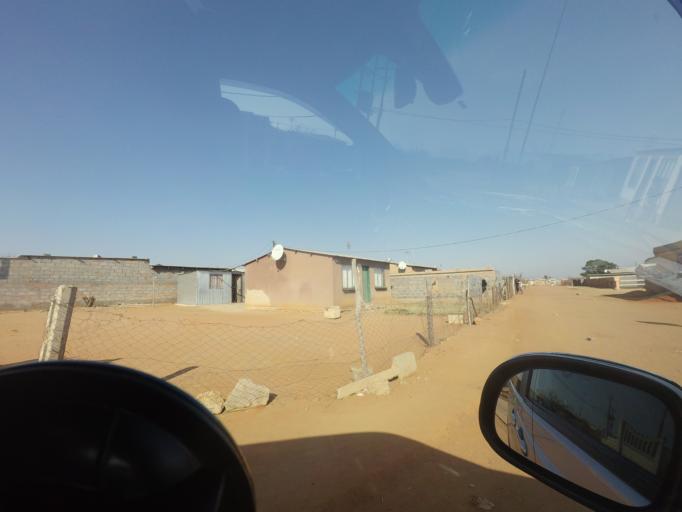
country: ZA
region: Gauteng
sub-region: Sedibeng District Municipality
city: Heidelberg
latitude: -26.5368
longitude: 28.3595
